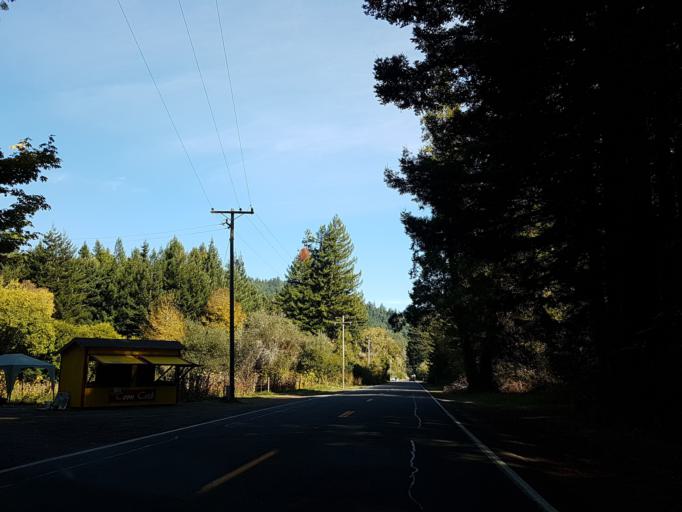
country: US
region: California
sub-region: Humboldt County
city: Rio Dell
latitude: 40.4461
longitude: -123.9998
